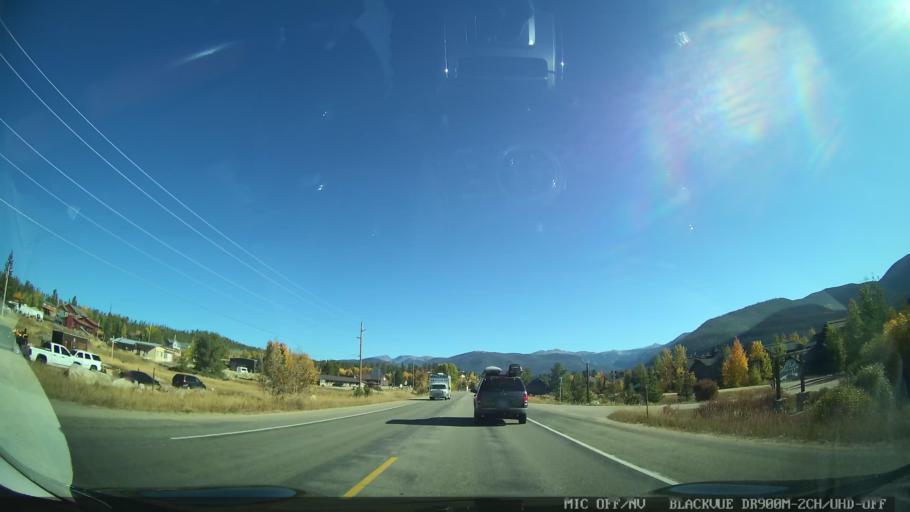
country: US
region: Colorado
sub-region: Grand County
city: Granby
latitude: 40.2222
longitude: -105.8564
